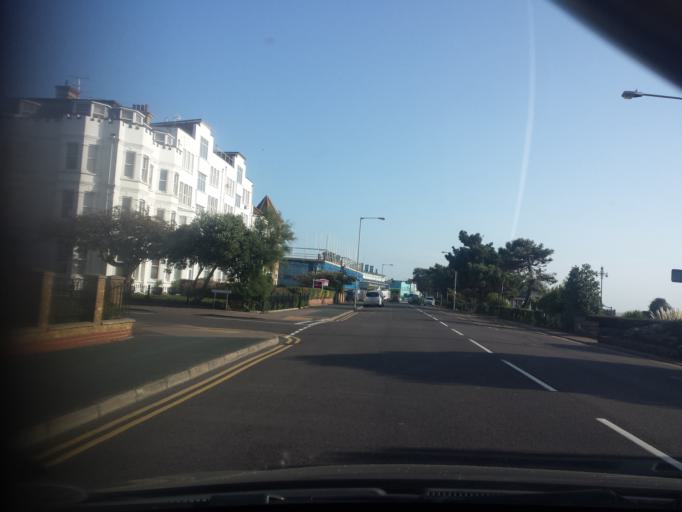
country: GB
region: England
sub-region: Essex
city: Clacton-on-Sea
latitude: 51.7861
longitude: 1.1513
